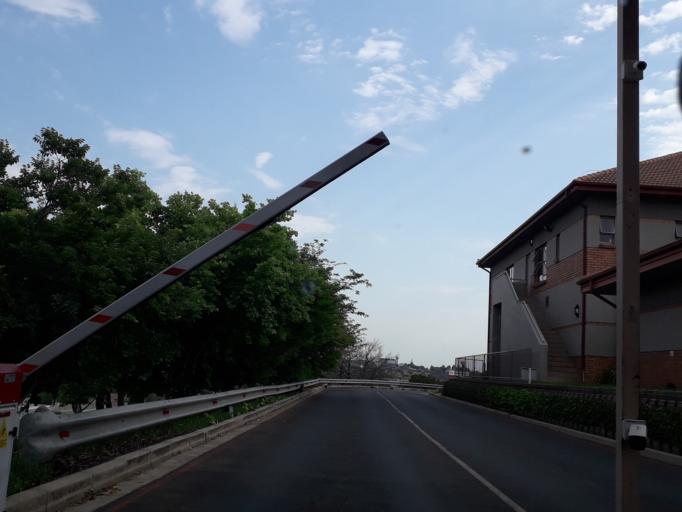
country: ZA
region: Gauteng
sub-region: City of Johannesburg Metropolitan Municipality
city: Roodepoort
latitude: -26.0992
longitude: 27.9245
